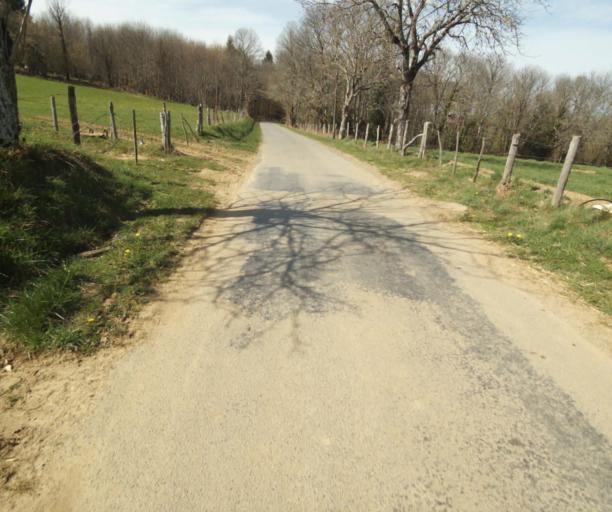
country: FR
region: Limousin
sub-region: Departement de la Correze
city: Naves
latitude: 45.3596
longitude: 1.7786
